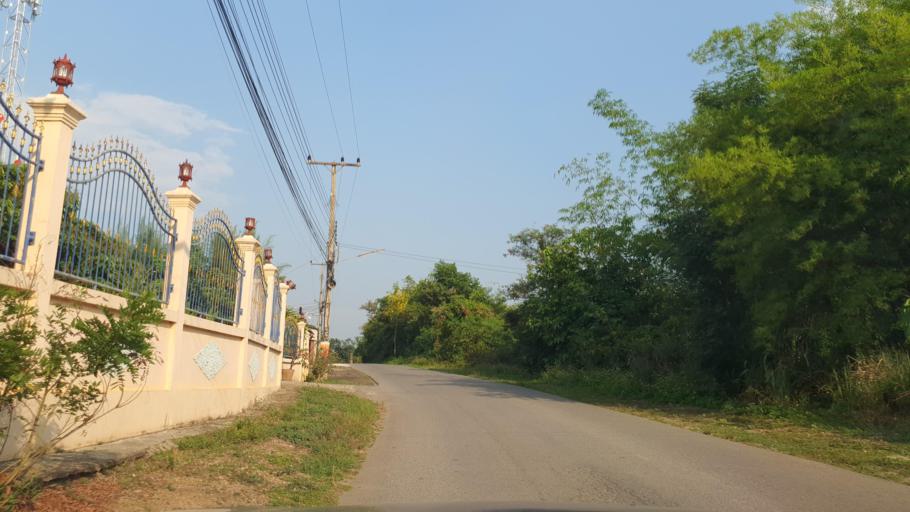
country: TH
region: Chiang Mai
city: Mae Wang
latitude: 18.6676
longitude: 98.8162
